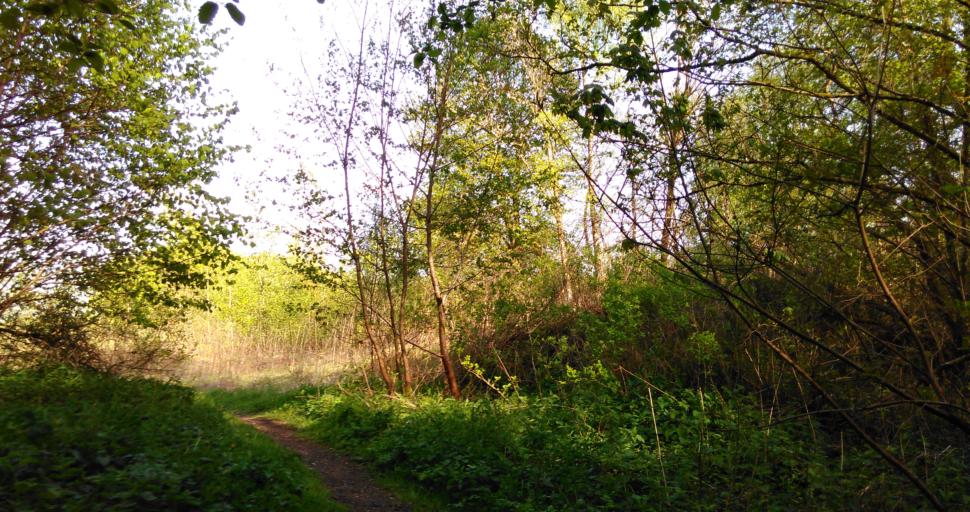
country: FR
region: Lorraine
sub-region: Departement de Meurthe-et-Moselle
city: Thil
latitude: 49.4950
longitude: 5.9086
